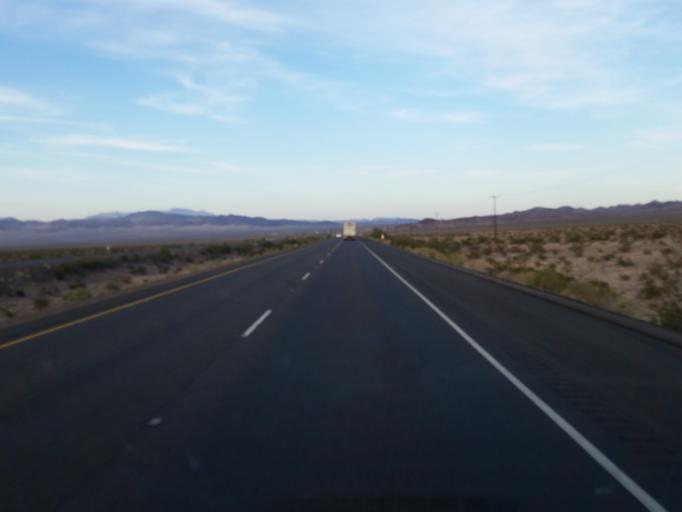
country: US
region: California
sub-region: San Bernardino County
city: Joshua Tree
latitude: 34.7253
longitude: -116.2237
